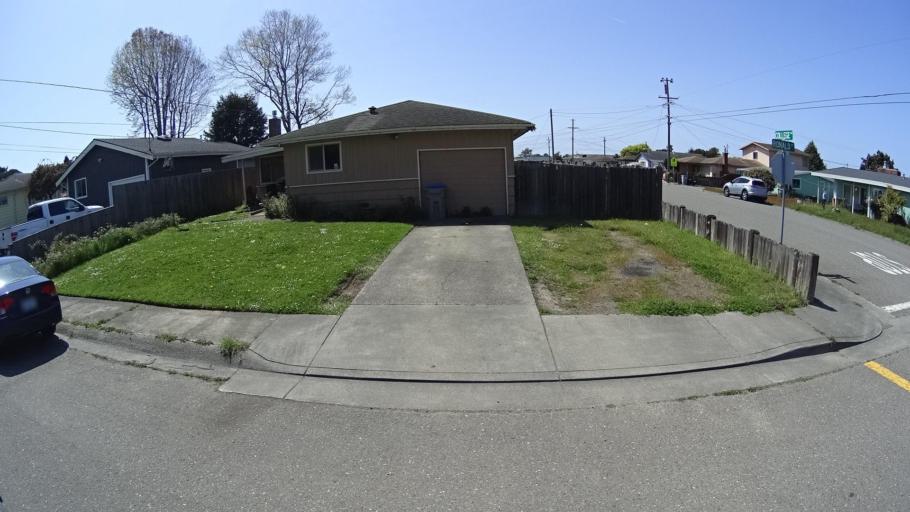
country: US
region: California
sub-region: Humboldt County
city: Fortuna
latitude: 40.5682
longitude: -124.1339
